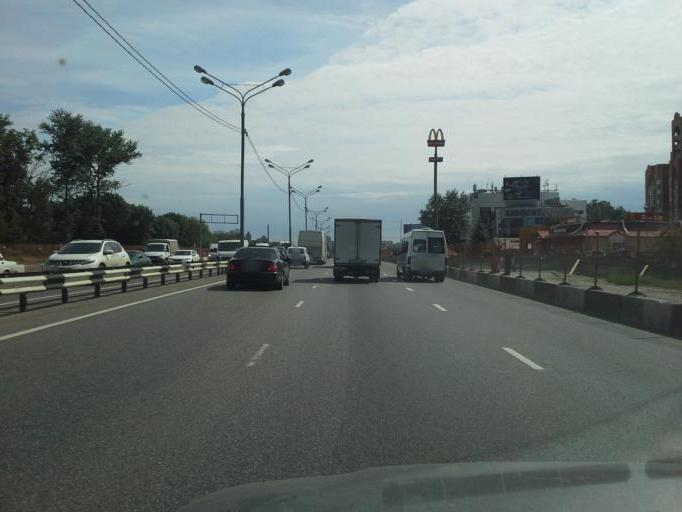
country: RU
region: Moskovskaya
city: Saltykovka
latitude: 55.7940
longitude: 37.9351
